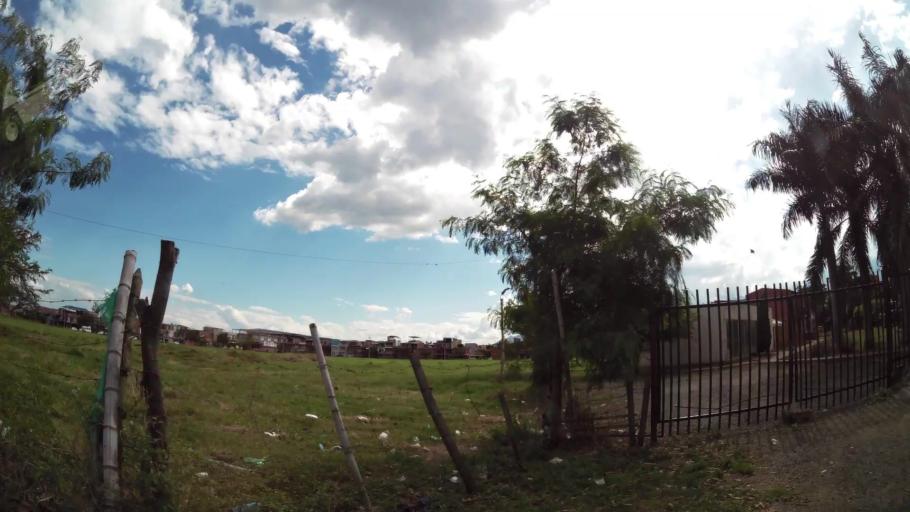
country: CO
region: Valle del Cauca
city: Cali
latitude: 3.3983
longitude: -76.5074
